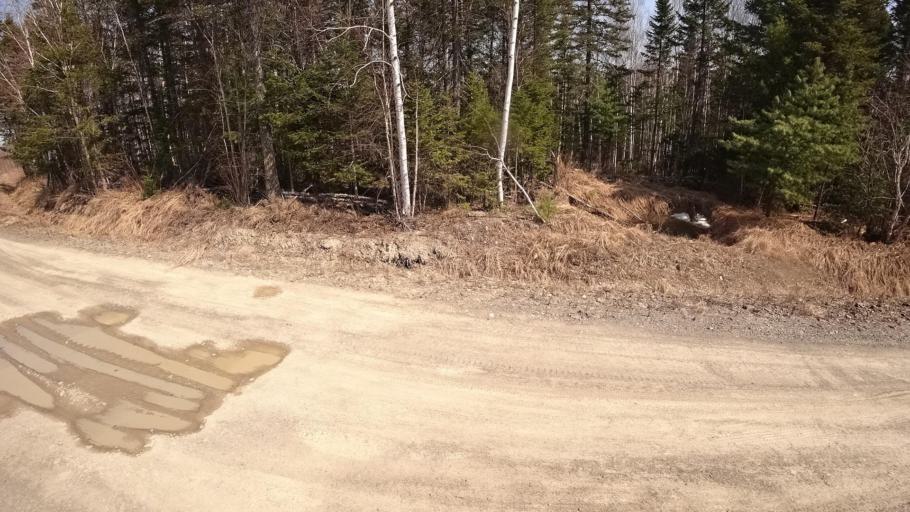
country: RU
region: Khabarovsk Krai
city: Selikhino
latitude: 50.6229
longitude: 137.3998
